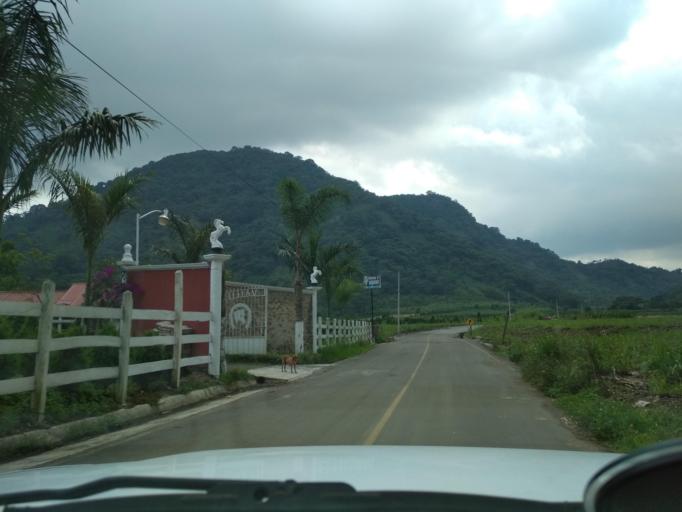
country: MX
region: Veracruz
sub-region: Fortin
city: Santa Lucia Potrerillo
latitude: 18.9471
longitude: -97.0608
